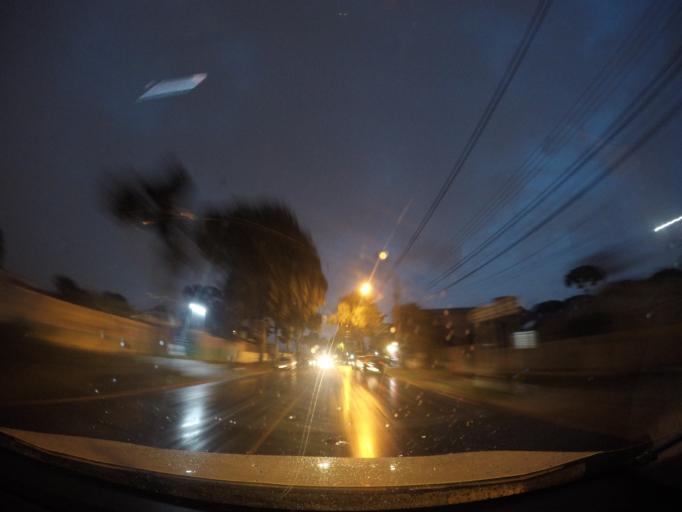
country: BR
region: Parana
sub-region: Sao Jose Dos Pinhais
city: Sao Jose dos Pinhais
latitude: -25.4975
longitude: -49.2464
